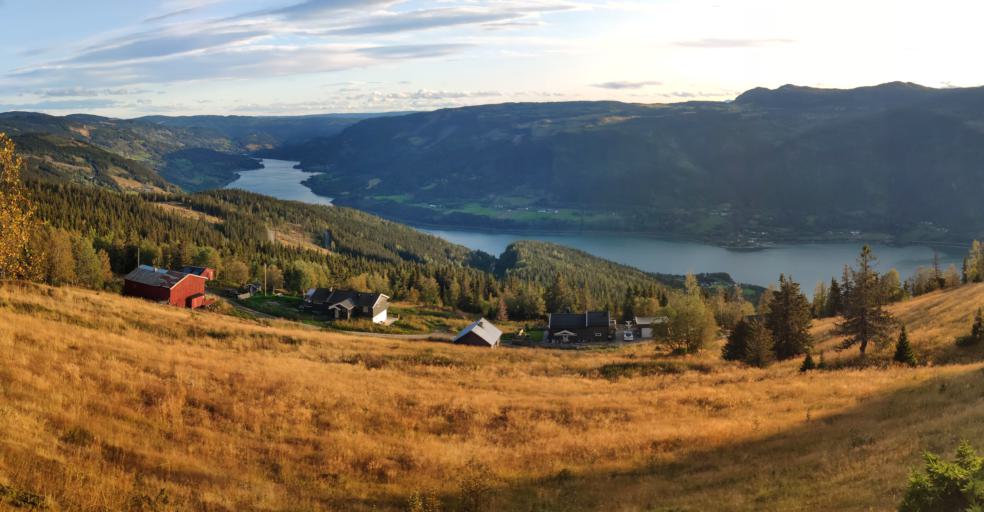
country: NO
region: Oppland
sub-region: Oyer
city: Tretten
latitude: 61.4099
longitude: 10.2626
